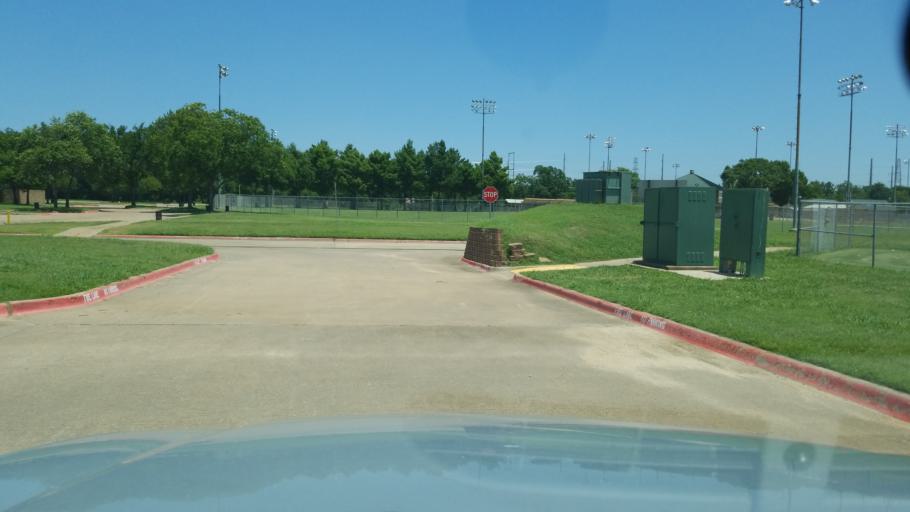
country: US
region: Texas
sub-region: Dallas County
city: Irving
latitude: 32.8114
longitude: -96.9127
